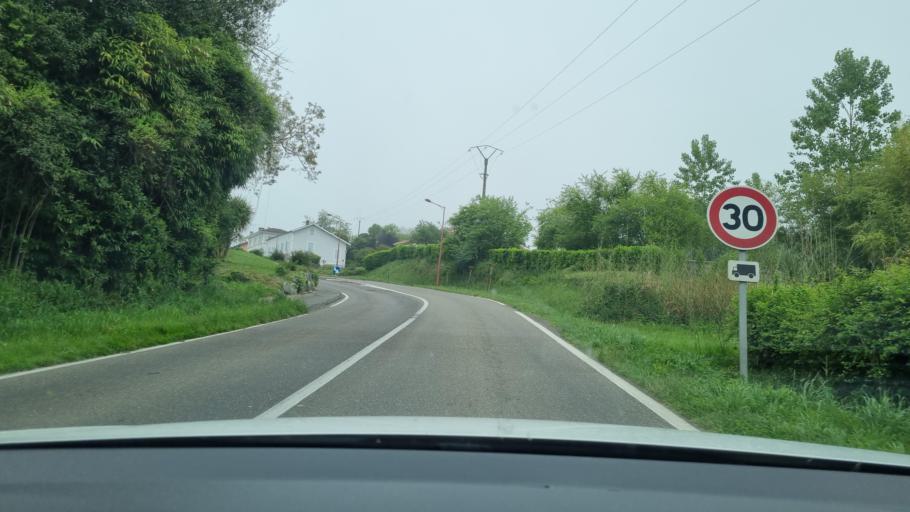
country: FR
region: Aquitaine
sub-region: Departement des Landes
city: Hagetmau
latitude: 43.6127
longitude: -0.6366
